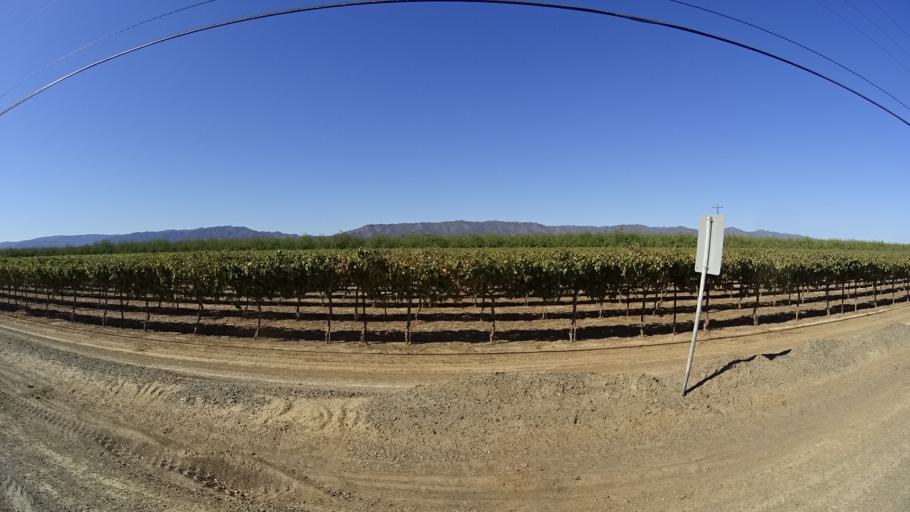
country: US
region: California
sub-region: Yolo County
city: Winters
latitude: 38.5418
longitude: -121.9712
